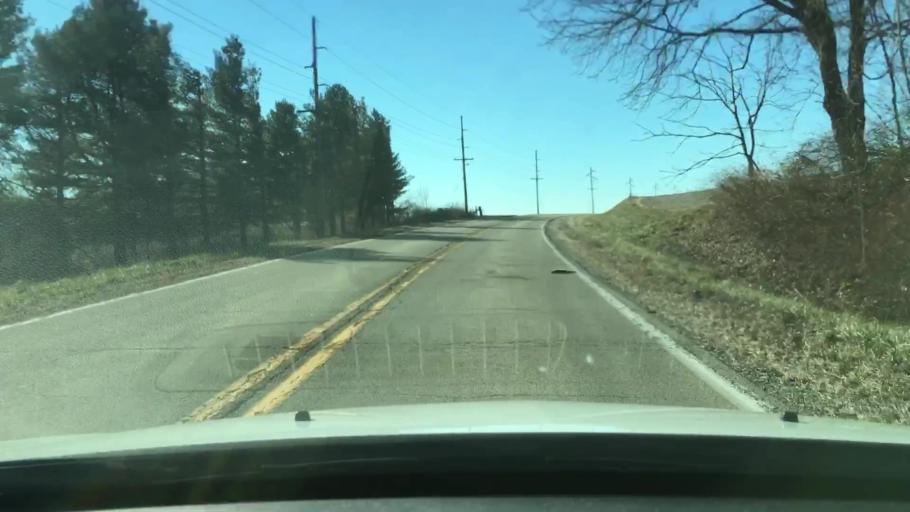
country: US
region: Illinois
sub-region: Fulton County
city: Astoria
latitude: 40.1864
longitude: -90.2117
